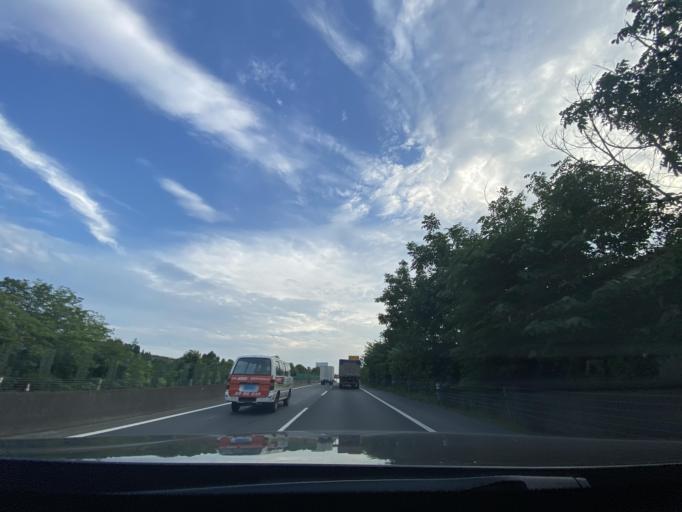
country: CN
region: Sichuan
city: Luojiang
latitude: 31.4087
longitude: 104.5770
